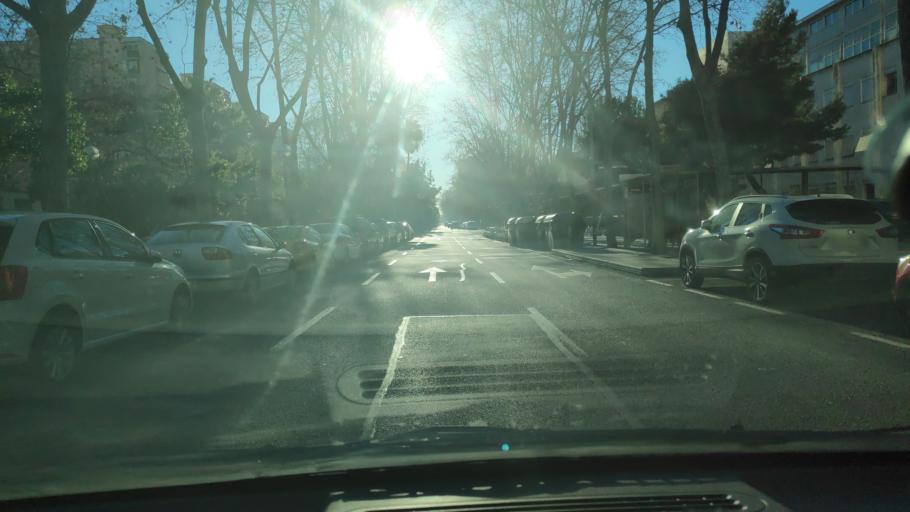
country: ES
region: Catalonia
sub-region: Provincia de Barcelona
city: Sant Marti
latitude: 41.4165
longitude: 2.2121
